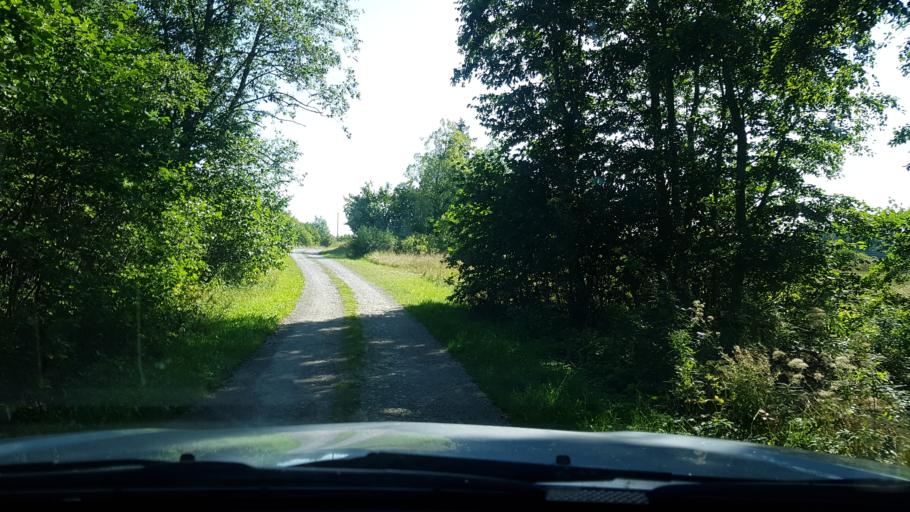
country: EE
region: Ida-Virumaa
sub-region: Sillamaee linn
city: Sillamae
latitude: 59.3943
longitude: 27.8775
